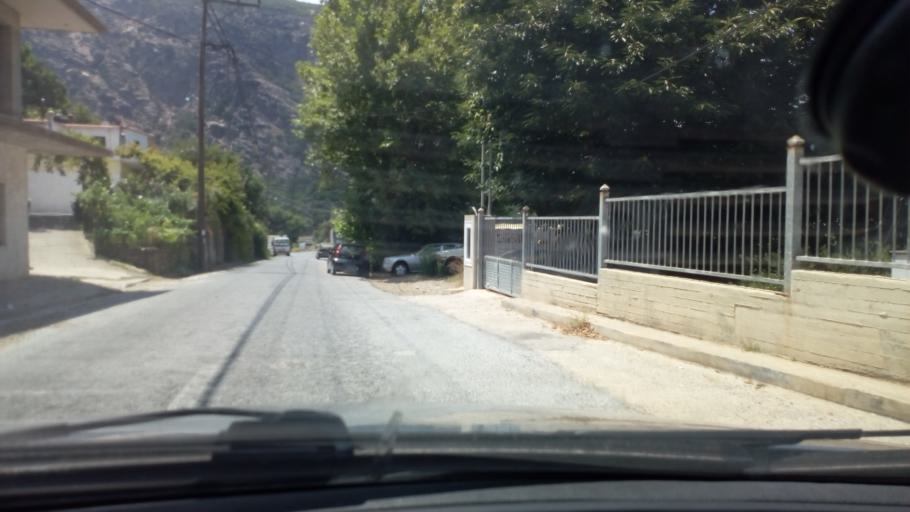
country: GR
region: North Aegean
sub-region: Nomos Samou
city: Agios Kirykos
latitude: 37.6413
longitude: 26.2605
